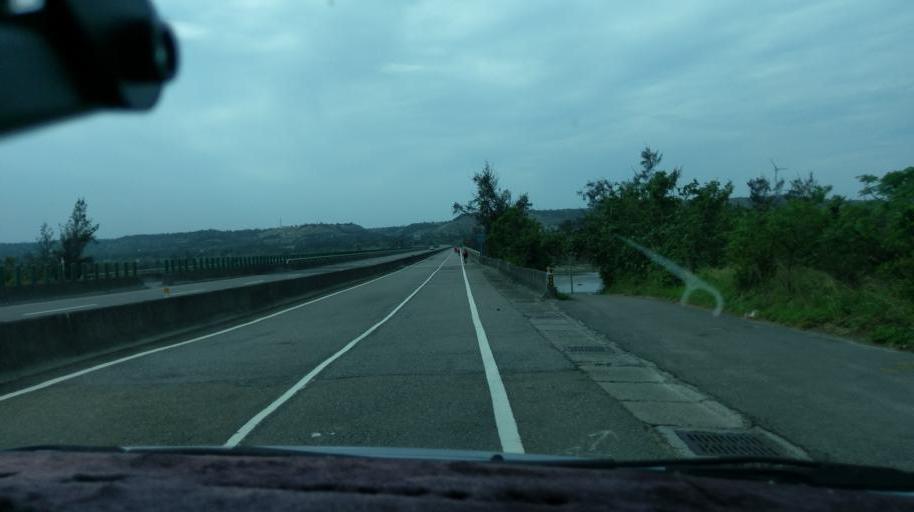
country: TW
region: Taiwan
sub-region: Miaoli
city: Miaoli
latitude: 24.6072
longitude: 120.7490
